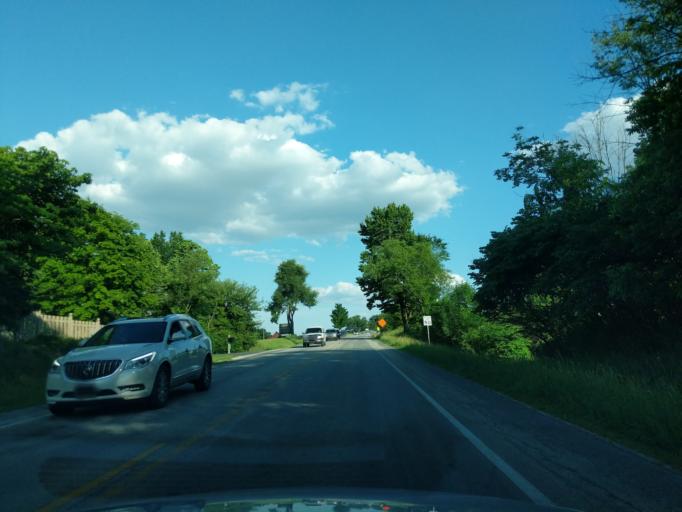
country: US
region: Indiana
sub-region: Whitley County
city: Columbia City
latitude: 41.1428
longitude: -85.4848
